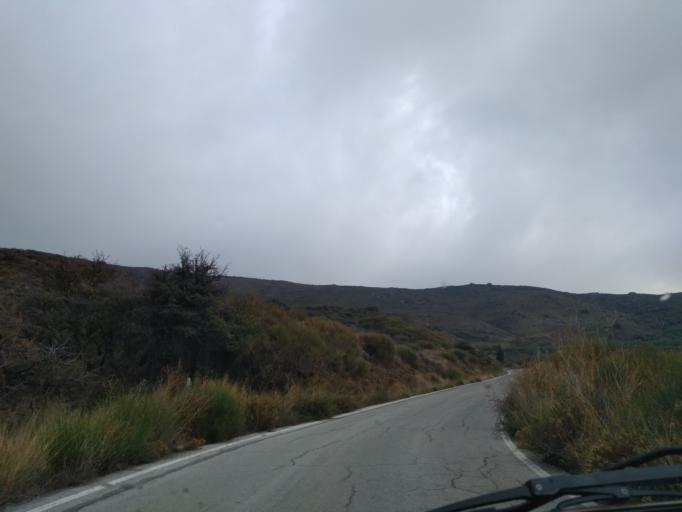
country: GR
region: Crete
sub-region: Nomos Lasithiou
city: Siteia
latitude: 35.1446
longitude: 26.0229
